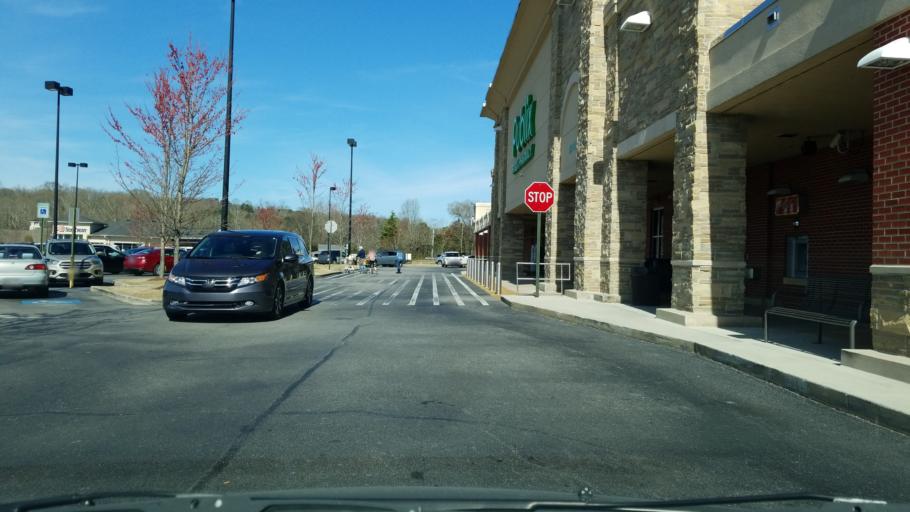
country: US
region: Tennessee
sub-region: Hamilton County
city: Collegedale
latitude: 35.0902
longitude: -85.0643
